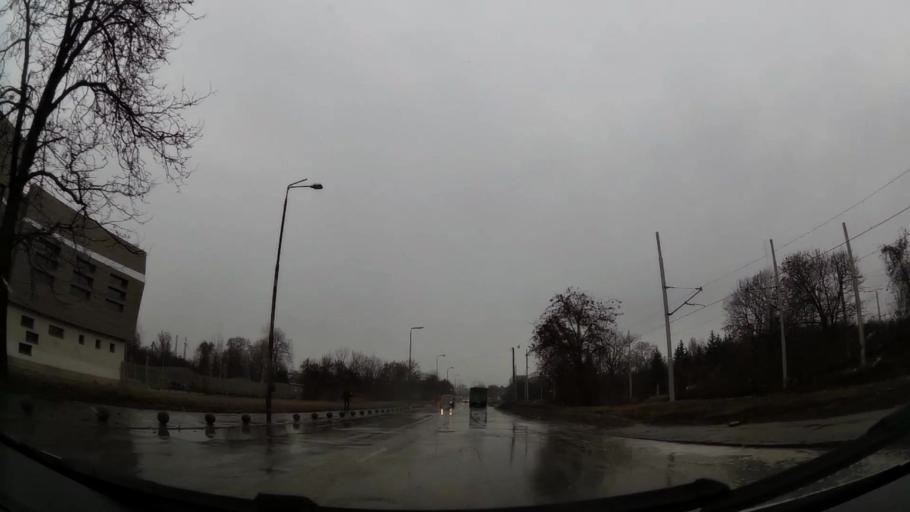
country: BG
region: Sofia-Capital
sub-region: Stolichna Obshtina
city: Sofia
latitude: 42.6636
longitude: 23.4126
